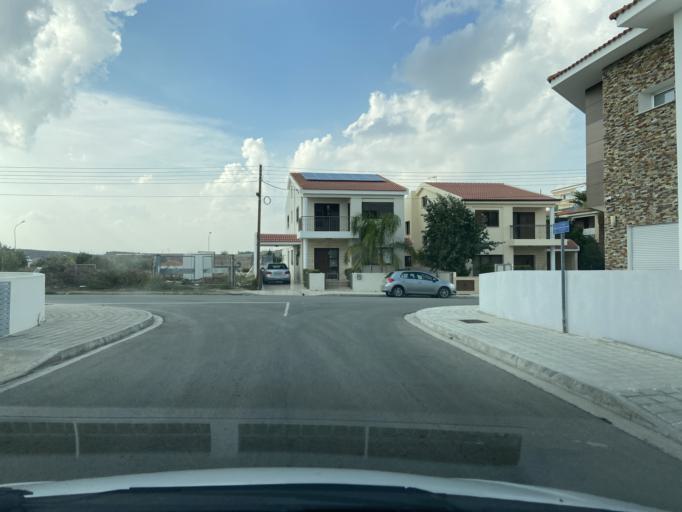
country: CY
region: Lefkosia
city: Dali
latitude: 35.0613
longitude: 33.3982
